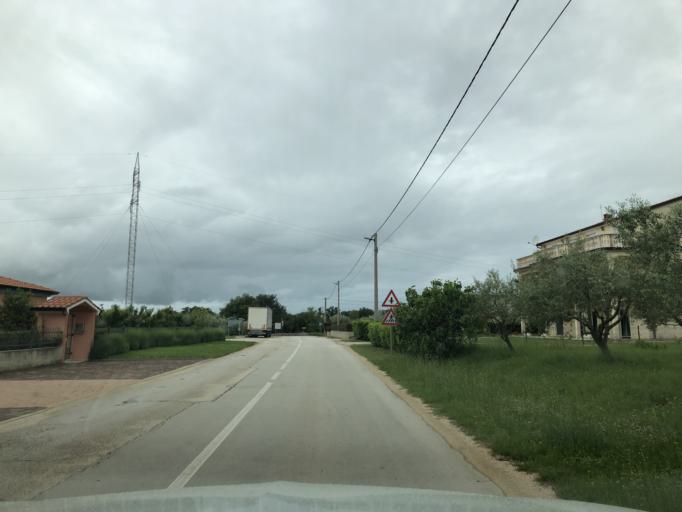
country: HR
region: Istarska
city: Buje
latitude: 45.4430
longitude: 13.6508
